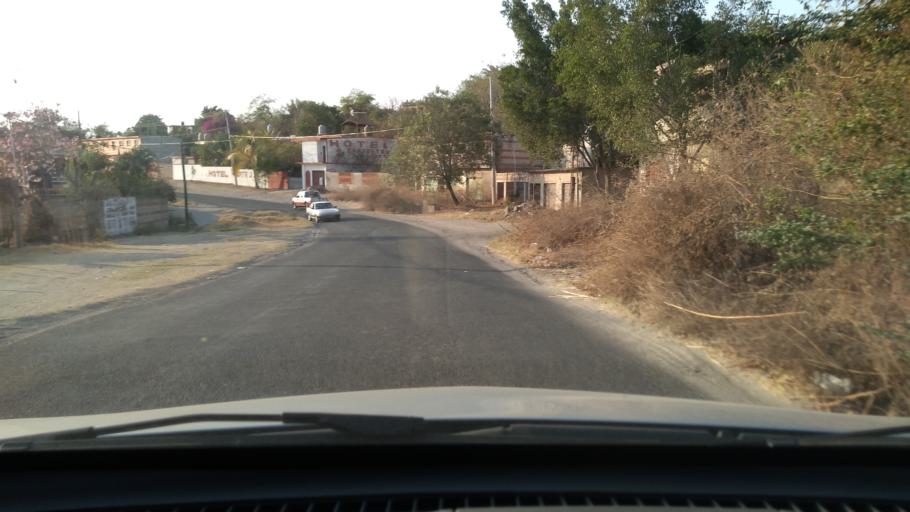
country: MX
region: Morelos
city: Puente de Ixtla
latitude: 18.6061
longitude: -99.3152
